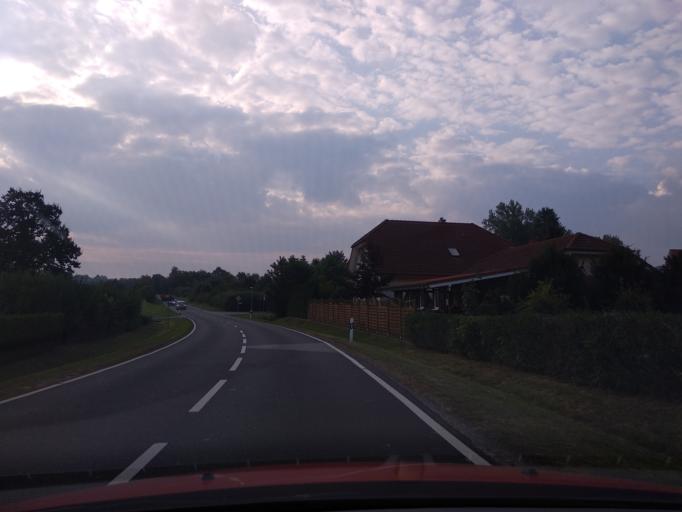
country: DE
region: Hesse
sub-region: Regierungsbezirk Kassel
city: Calden
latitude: 51.3936
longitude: 9.3509
